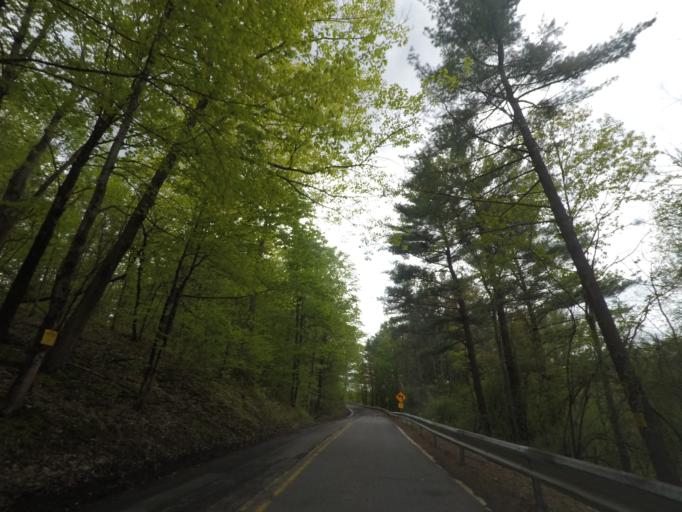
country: US
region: New York
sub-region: Albany County
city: Voorheesville
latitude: 42.6898
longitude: -73.9251
